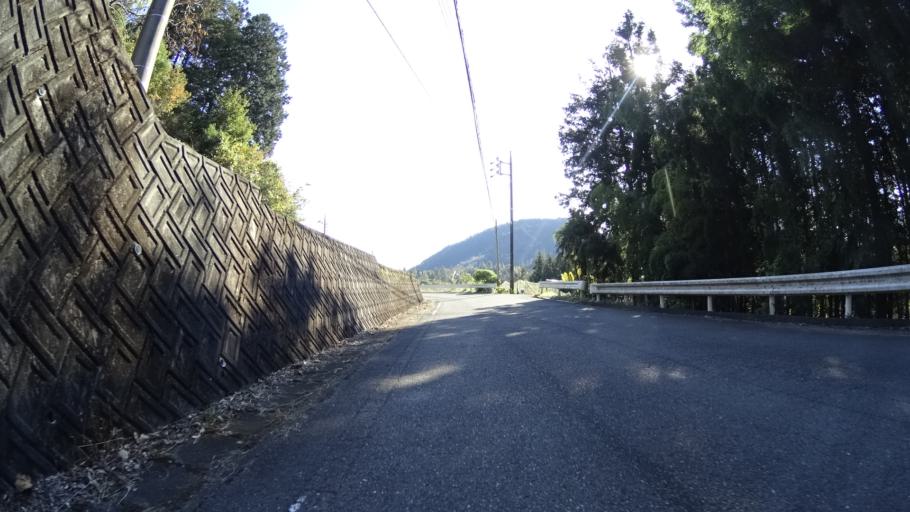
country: JP
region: Yamanashi
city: Uenohara
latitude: 35.6687
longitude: 139.1017
